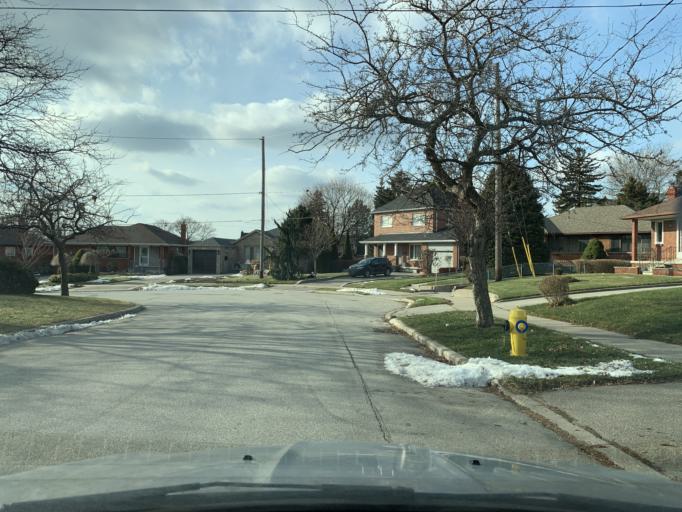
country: CA
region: Ontario
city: Toronto
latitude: 43.7045
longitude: -79.4855
